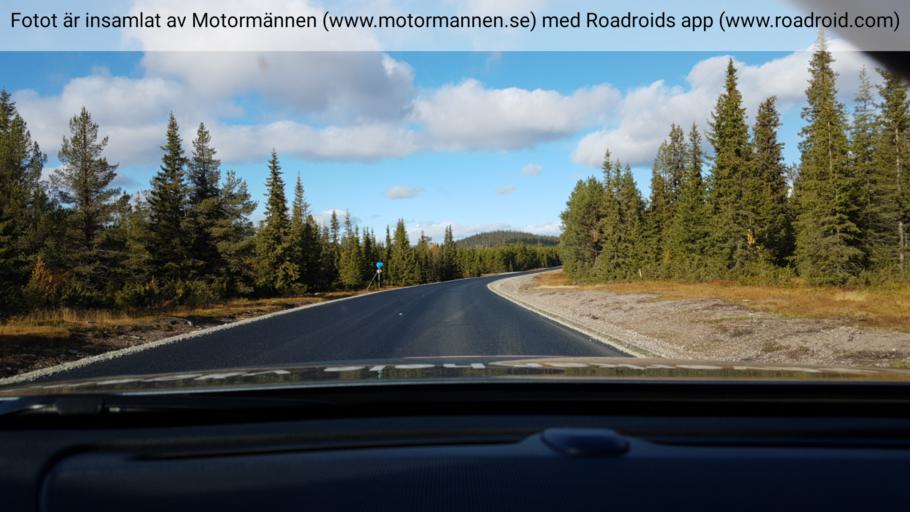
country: SE
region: Norrbotten
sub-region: Arjeplogs Kommun
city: Arjeplog
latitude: 65.9165
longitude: 18.3250
